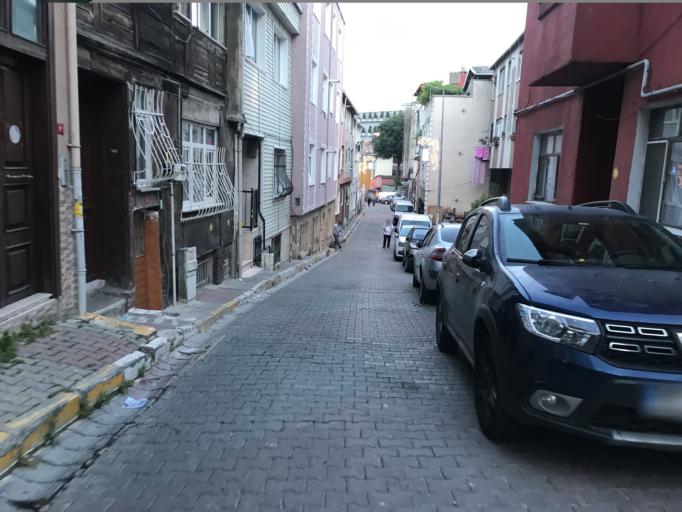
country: TR
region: Istanbul
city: Istanbul
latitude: 41.0401
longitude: 28.9312
